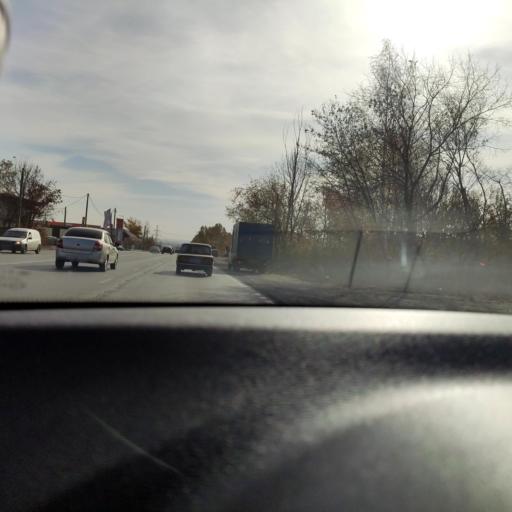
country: RU
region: Samara
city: Petra-Dubrava
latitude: 53.2658
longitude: 50.2838
